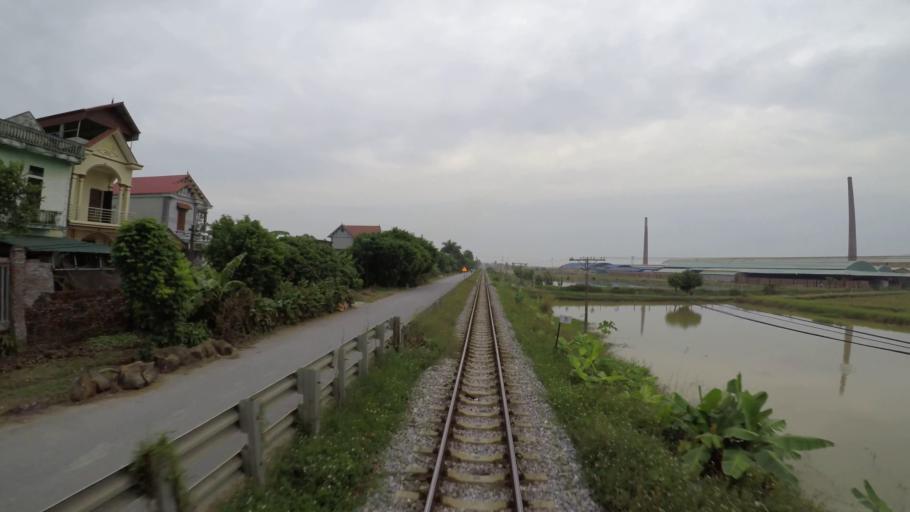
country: VN
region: Hai Duong
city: Ke Sat
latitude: 20.9654
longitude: 106.1168
